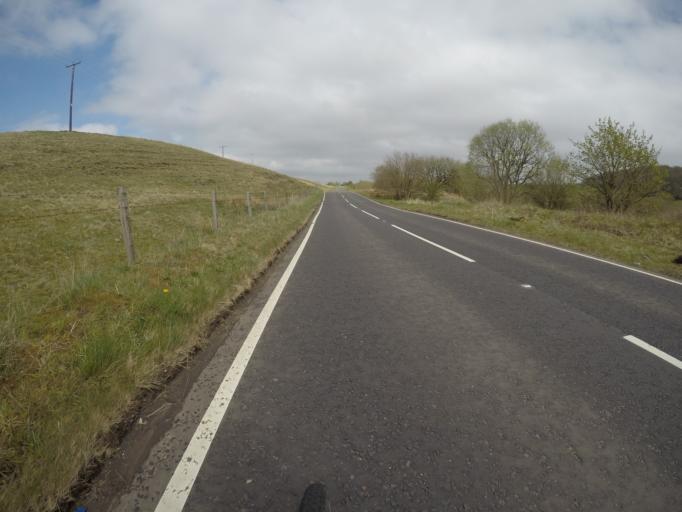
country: GB
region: Scotland
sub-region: East Renfrewshire
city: Neilston
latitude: 55.7301
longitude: -4.4200
